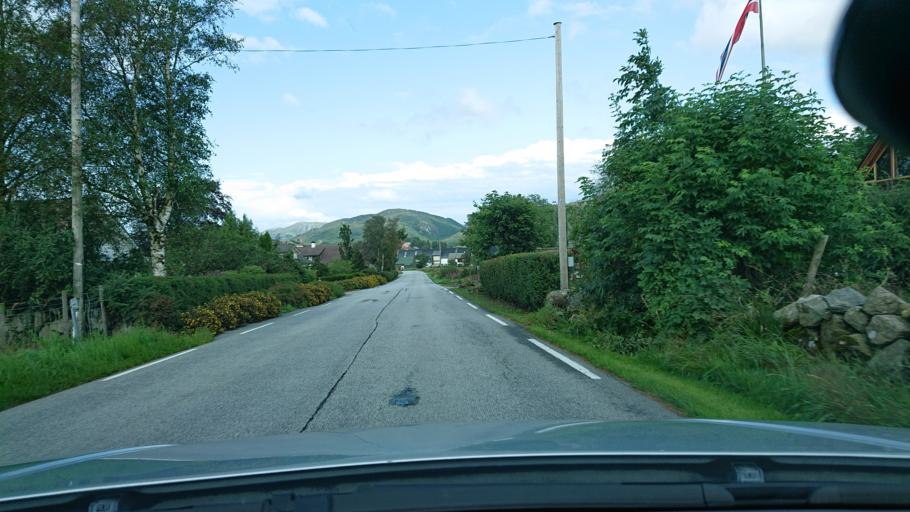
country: NO
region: Rogaland
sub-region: Gjesdal
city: Algard
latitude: 58.6951
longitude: 5.7780
